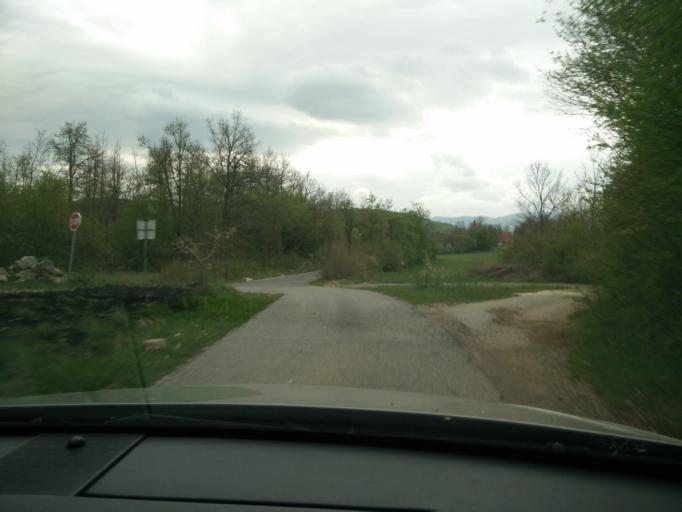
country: HR
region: Zadarska
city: Gracac
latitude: 44.3969
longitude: 15.6884
